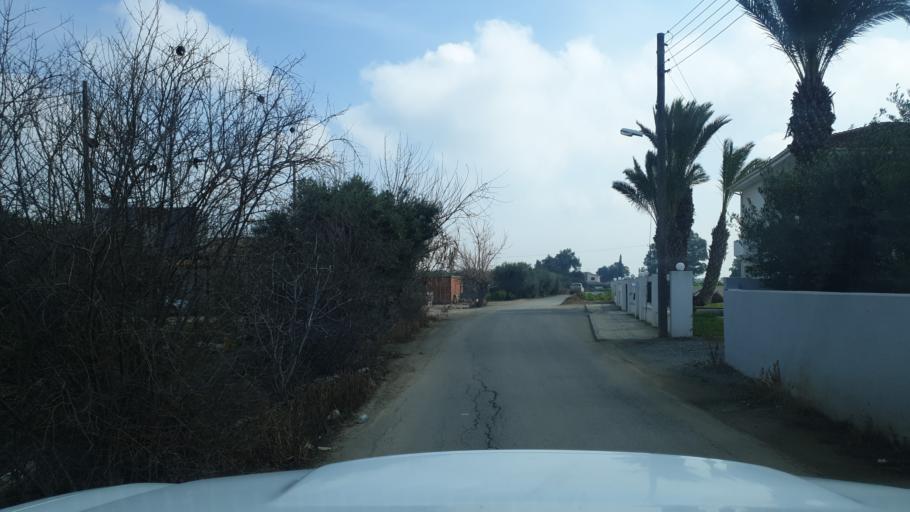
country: CY
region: Lefkosia
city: Kato Deftera
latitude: 35.0812
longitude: 33.2739
